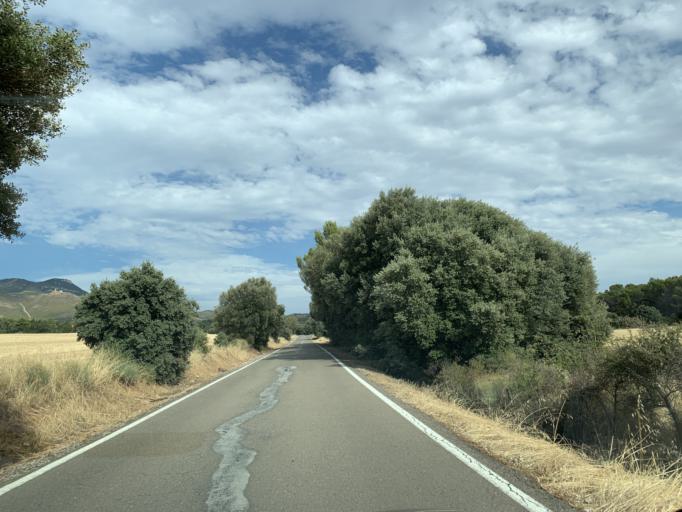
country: ES
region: Aragon
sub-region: Provincia de Zaragoza
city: Santa Eulalia de Gallego
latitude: 42.3152
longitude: -0.7373
